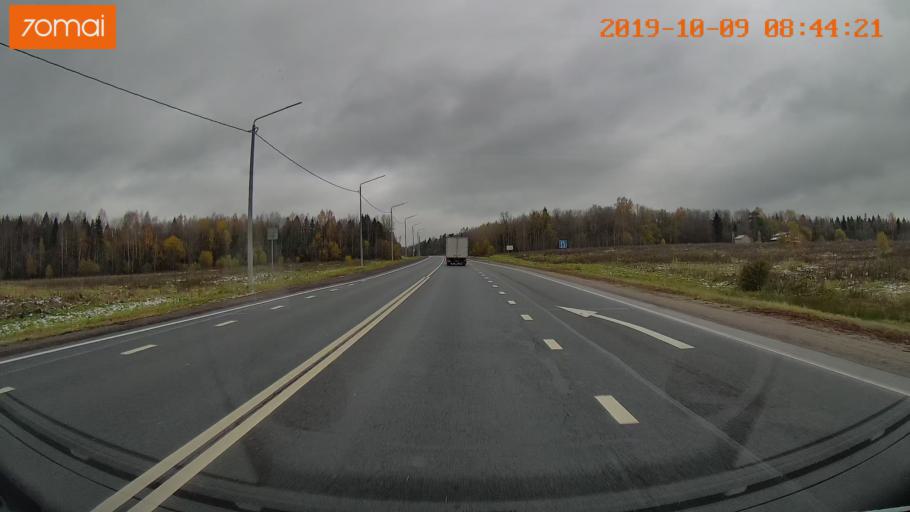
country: RU
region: Vologda
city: Gryazovets
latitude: 59.0356
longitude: 40.1085
